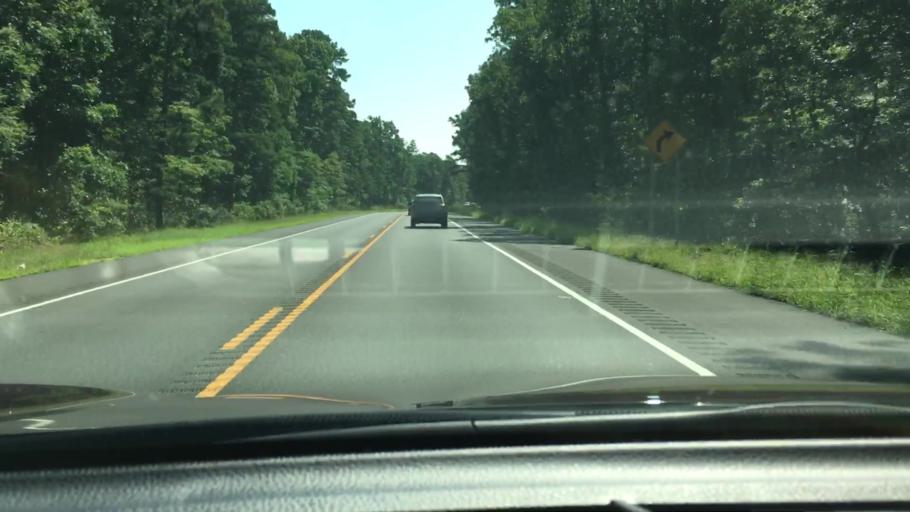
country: US
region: New Jersey
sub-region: Cape May County
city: Woodbine
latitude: 39.3164
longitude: -74.8367
